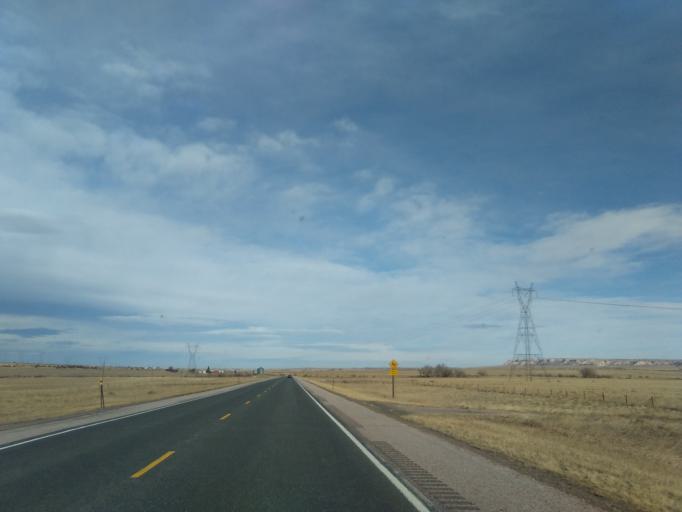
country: US
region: Wyoming
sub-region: Goshen County
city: Torrington
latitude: 41.6324
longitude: -104.2442
